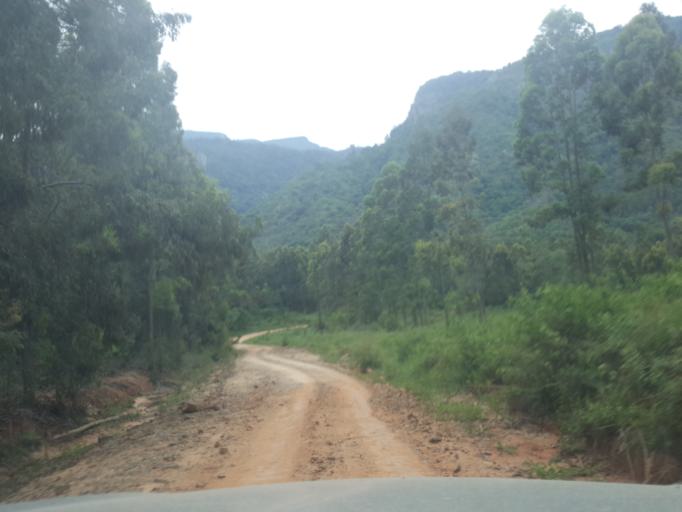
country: ZA
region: Limpopo
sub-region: Mopani District Municipality
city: Hoedspruit
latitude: -24.5938
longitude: 30.8813
